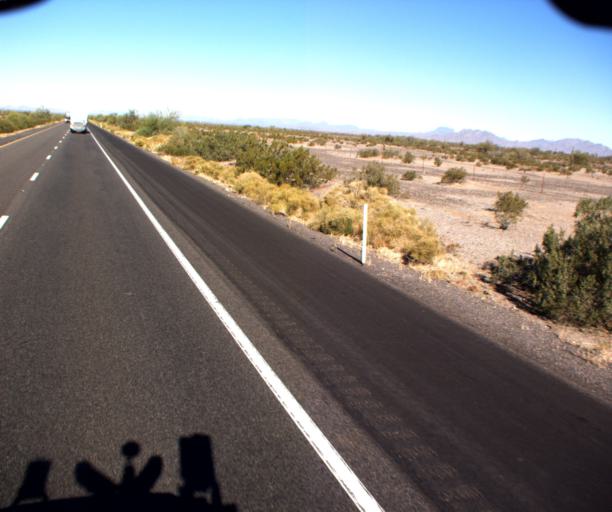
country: US
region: Arizona
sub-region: Maricopa County
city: Gila Bend
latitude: 32.9111
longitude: -112.6056
